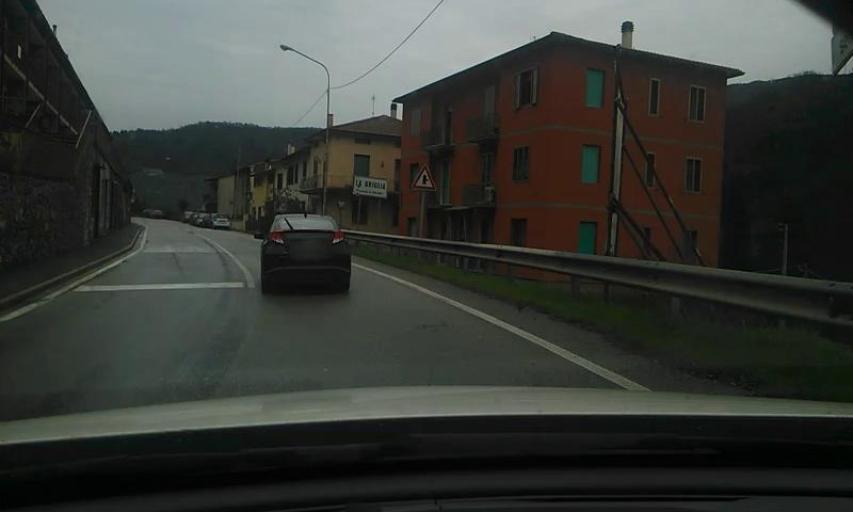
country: IT
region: Tuscany
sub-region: Provincia di Prato
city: Vaiano
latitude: 43.9320
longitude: 11.1263
